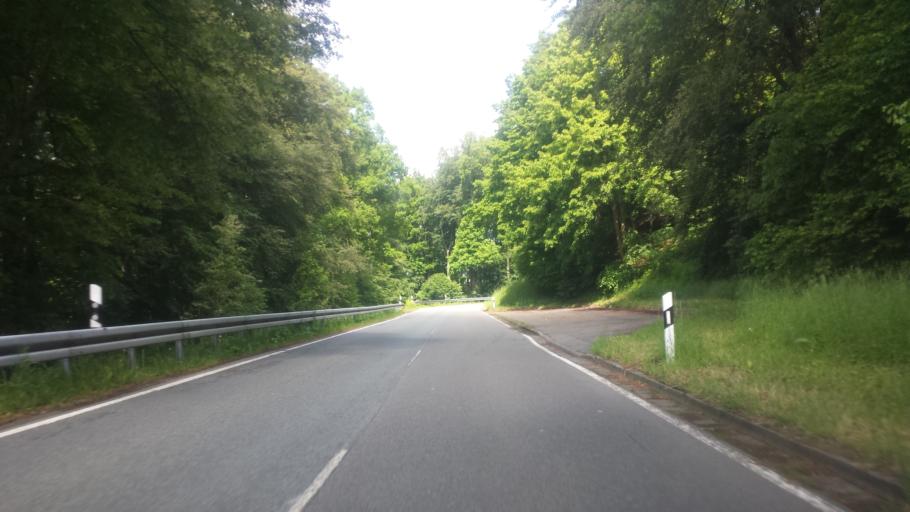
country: DE
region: Hesse
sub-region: Regierungsbezirk Darmstadt
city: Wald-Michelbach
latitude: 49.5737
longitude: 8.8007
